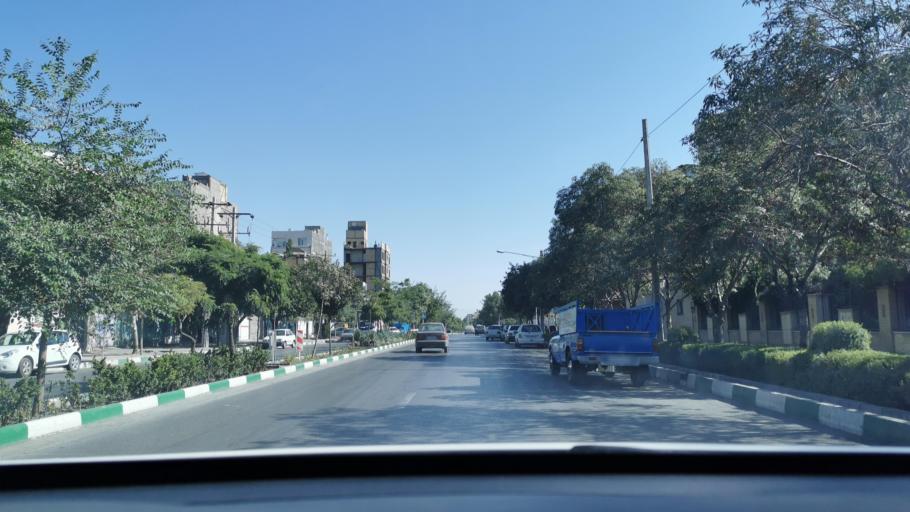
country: IR
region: Razavi Khorasan
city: Mashhad
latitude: 36.3323
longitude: 59.5913
